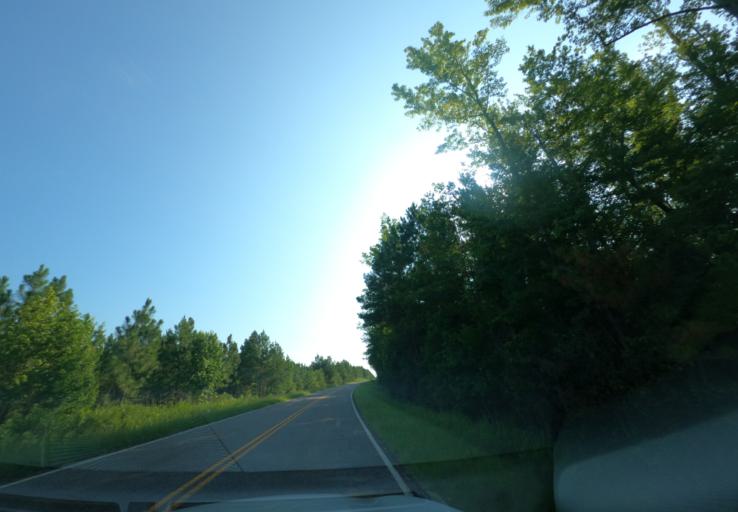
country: US
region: South Carolina
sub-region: Edgefield County
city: Edgefield
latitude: 33.7565
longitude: -81.9547
